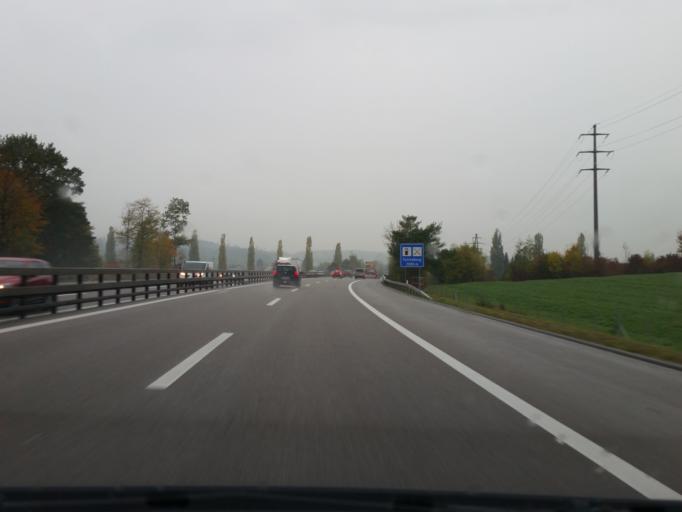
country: CH
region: Zurich
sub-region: Bezirk Winterthur
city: Oberwinterthur (Kreis 2)
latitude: 47.5282
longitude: 8.7647
